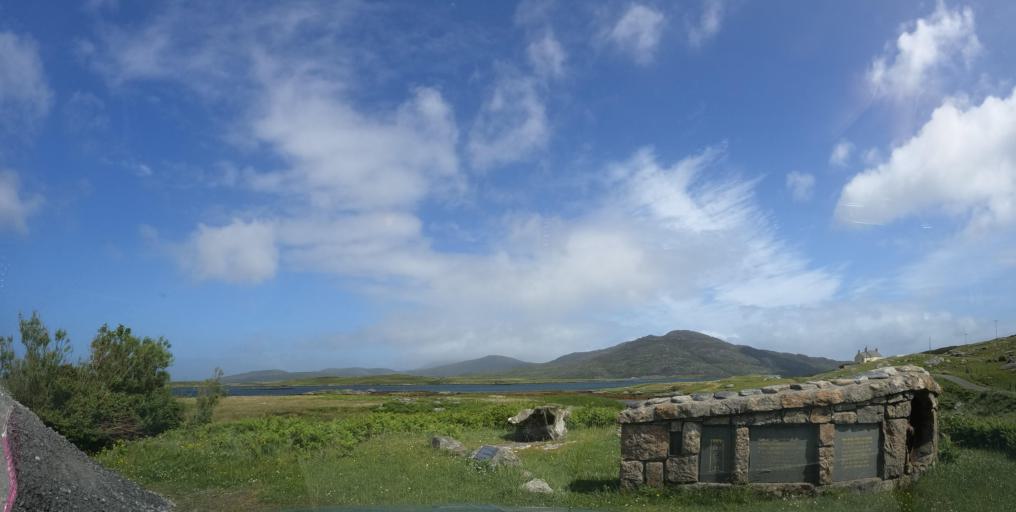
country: GB
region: Scotland
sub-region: Eilean Siar
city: Isle of South Uist
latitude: 57.1372
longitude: -7.3076
